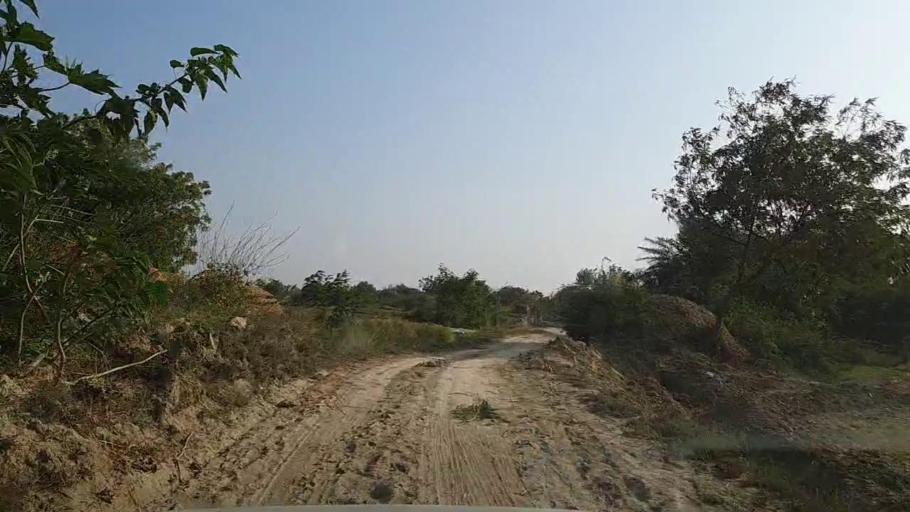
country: PK
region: Sindh
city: Mirpur Sakro
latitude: 24.5903
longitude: 67.6467
